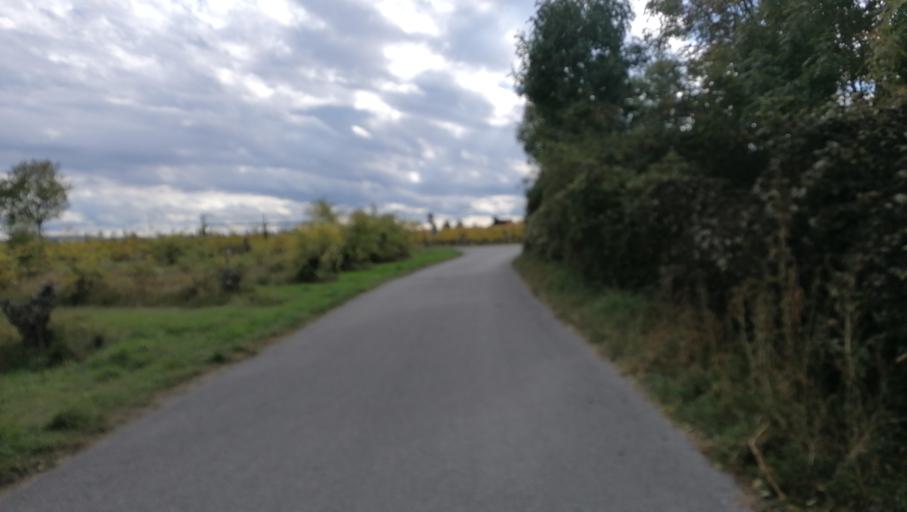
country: AT
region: Lower Austria
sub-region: Politischer Bezirk Baden
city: Tattendorf
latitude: 47.9554
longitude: 16.3088
